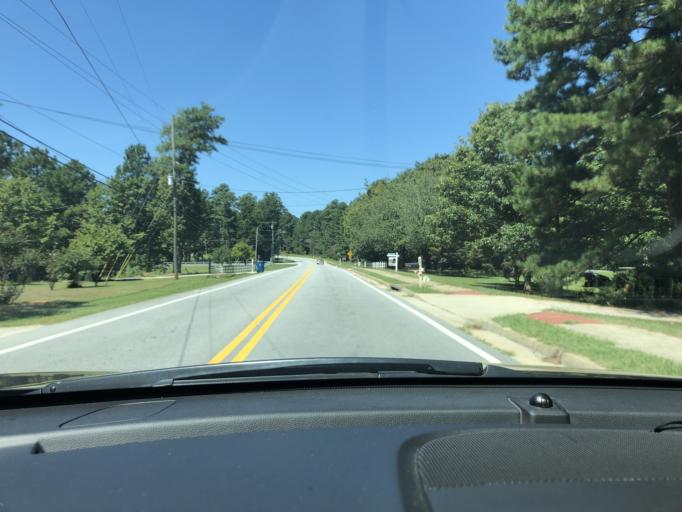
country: US
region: Georgia
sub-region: Gwinnett County
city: Grayson
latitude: 33.8956
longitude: -83.9036
